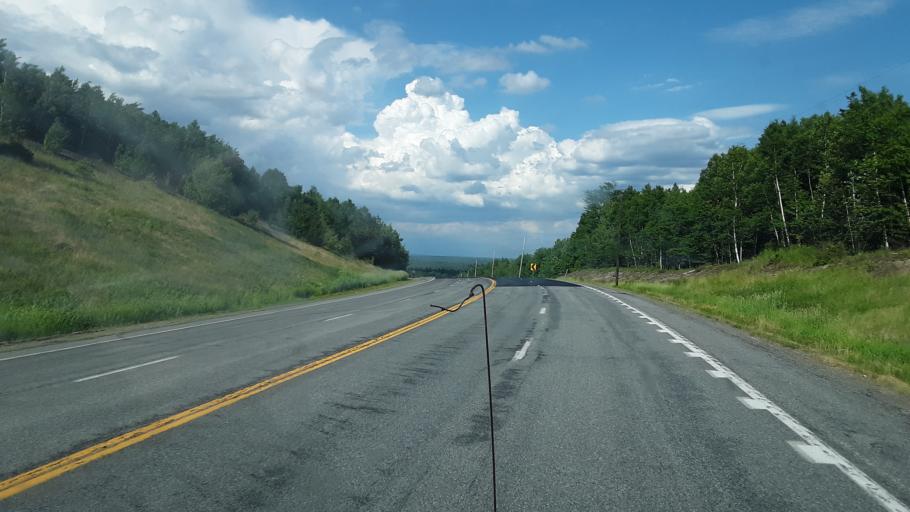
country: US
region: Maine
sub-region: Washington County
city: Cherryfield
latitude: 44.8648
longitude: -68.0049
